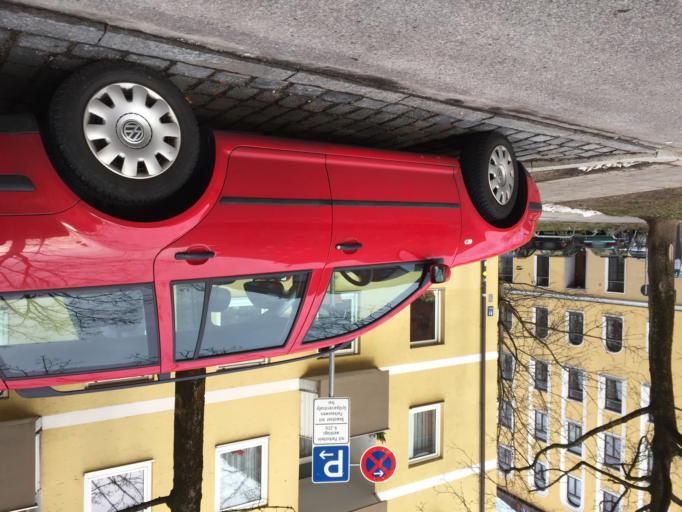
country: DE
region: Bavaria
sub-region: Upper Bavaria
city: Bogenhausen
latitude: 48.1330
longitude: 11.6077
